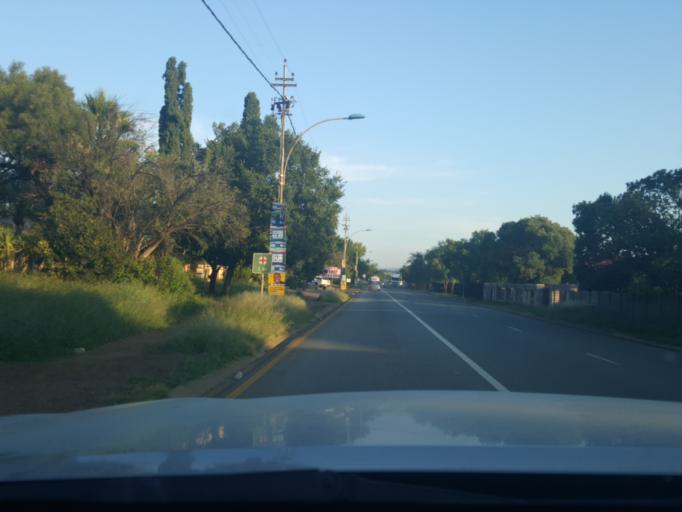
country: ZA
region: North-West
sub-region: Ngaka Modiri Molema District Municipality
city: Zeerust
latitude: -25.5344
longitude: 26.0767
